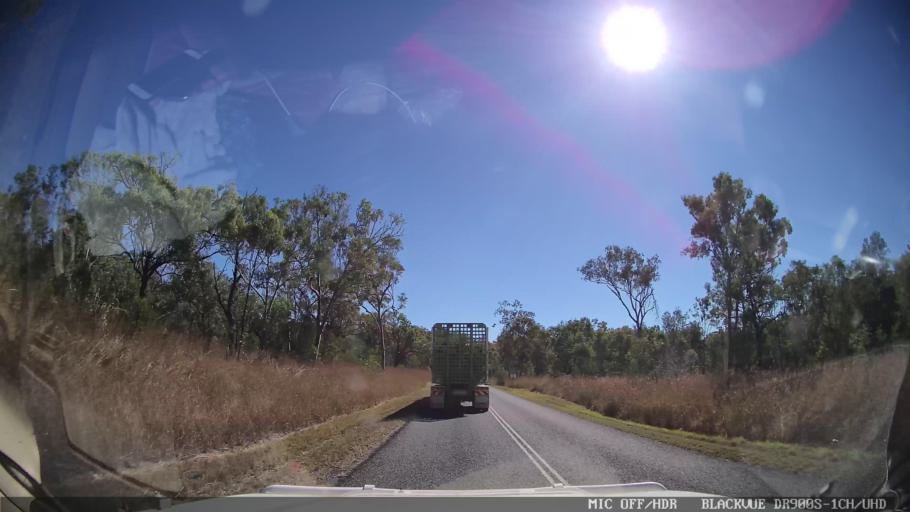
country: AU
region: Queensland
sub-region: Gladstone
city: Toolooa
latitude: -24.1494
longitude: 151.2080
